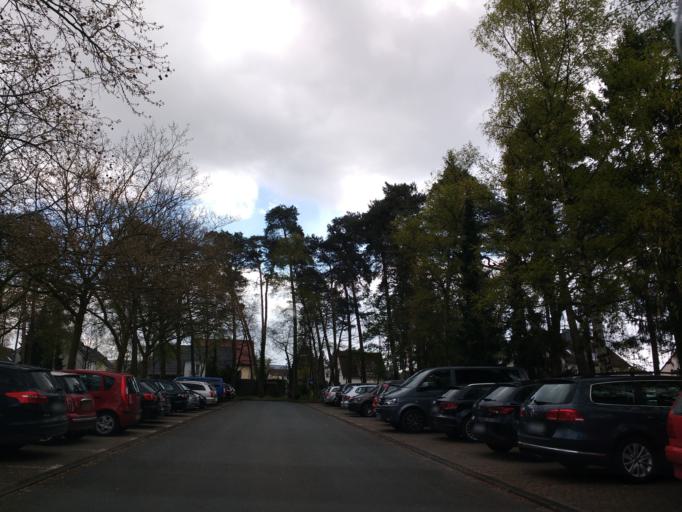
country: DE
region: North Rhine-Westphalia
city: Bad Lippspringe
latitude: 51.7918
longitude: 8.8239
